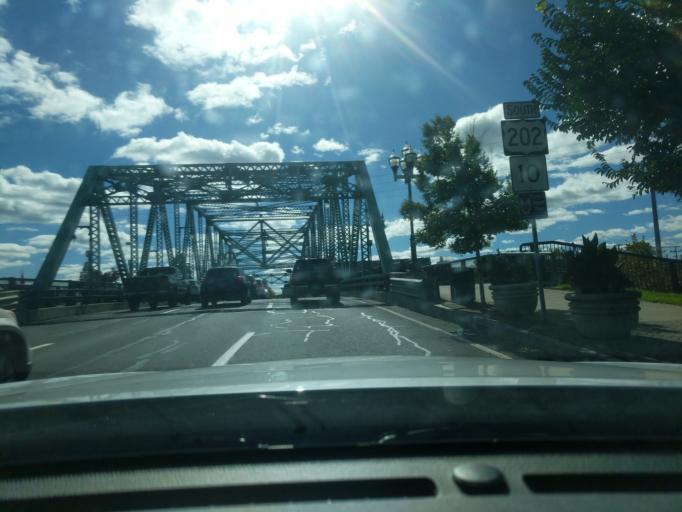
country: US
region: Massachusetts
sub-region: Hampden County
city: Westfield
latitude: 42.1295
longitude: -72.7459
